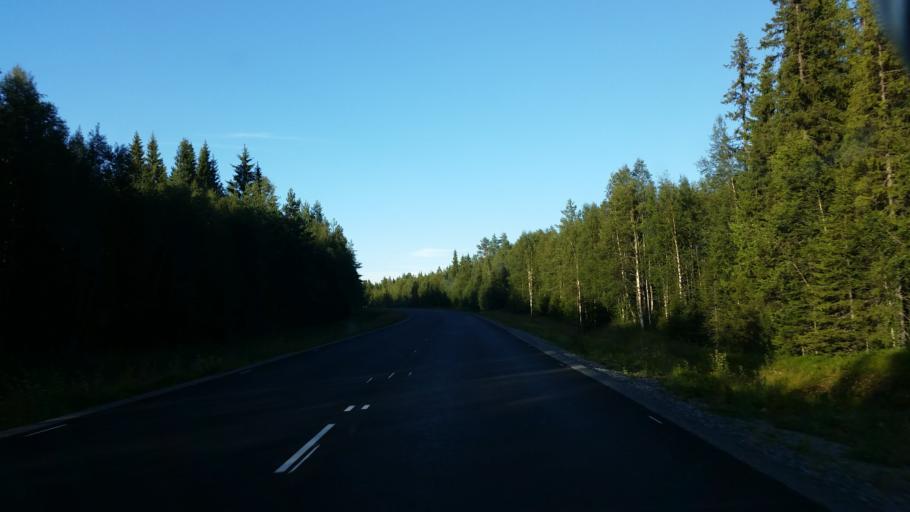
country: SE
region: Vaesterbotten
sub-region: Dorotea Kommun
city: Dorotea
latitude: 64.3025
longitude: 16.5836
